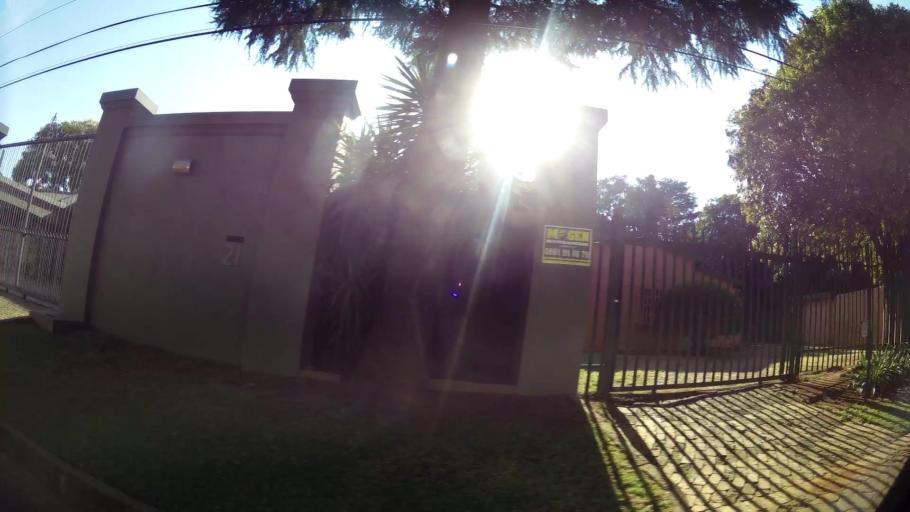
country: ZA
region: Gauteng
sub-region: Ekurhuleni Metropolitan Municipality
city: Germiston
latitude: -26.1714
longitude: 28.1416
